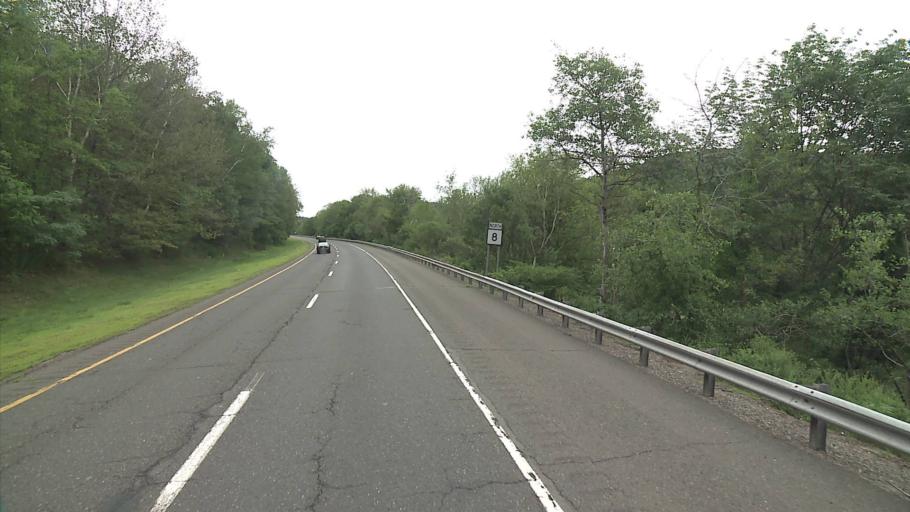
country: US
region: Connecticut
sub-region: Litchfield County
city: Oakville
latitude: 41.6193
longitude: -73.0632
